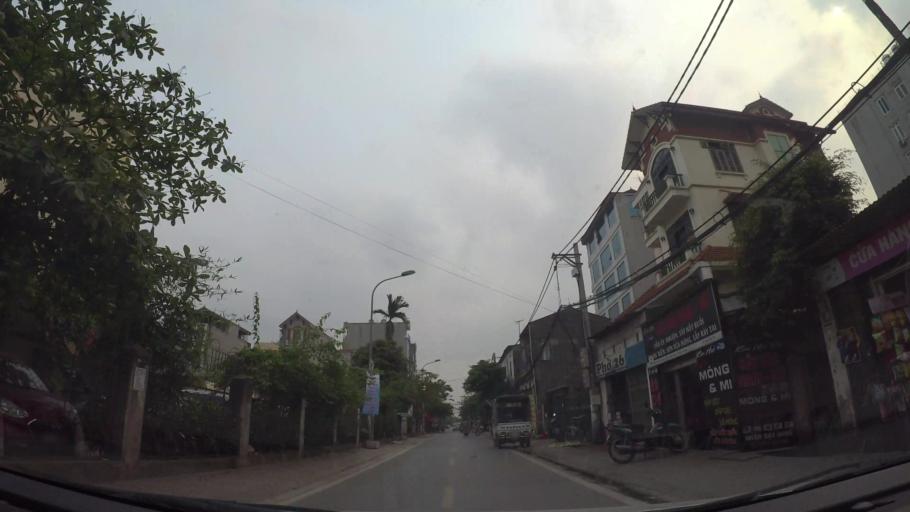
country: VN
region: Ha Noi
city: Cau Dien
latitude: 21.0442
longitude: 105.7527
